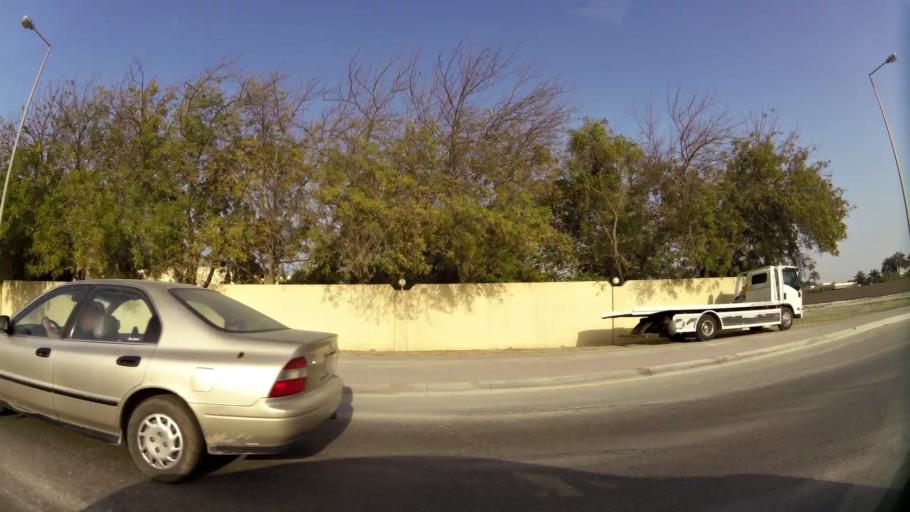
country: BH
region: Manama
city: Jidd Hafs
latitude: 26.2154
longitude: 50.4801
